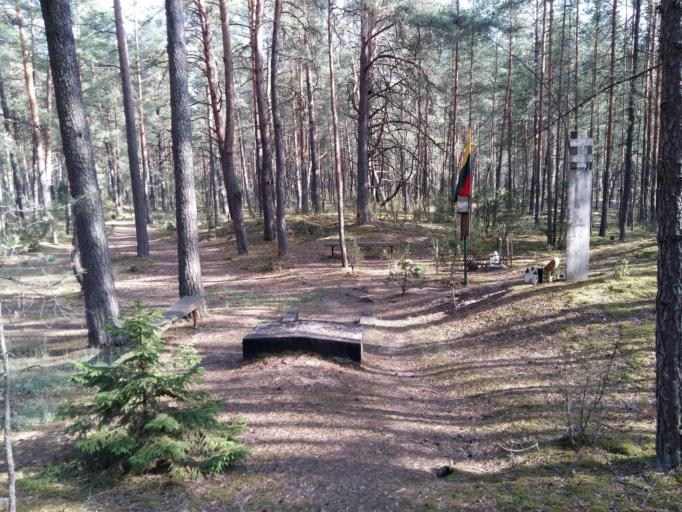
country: LT
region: Alytaus apskritis
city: Druskininkai
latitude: 54.0847
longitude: 24.2319
